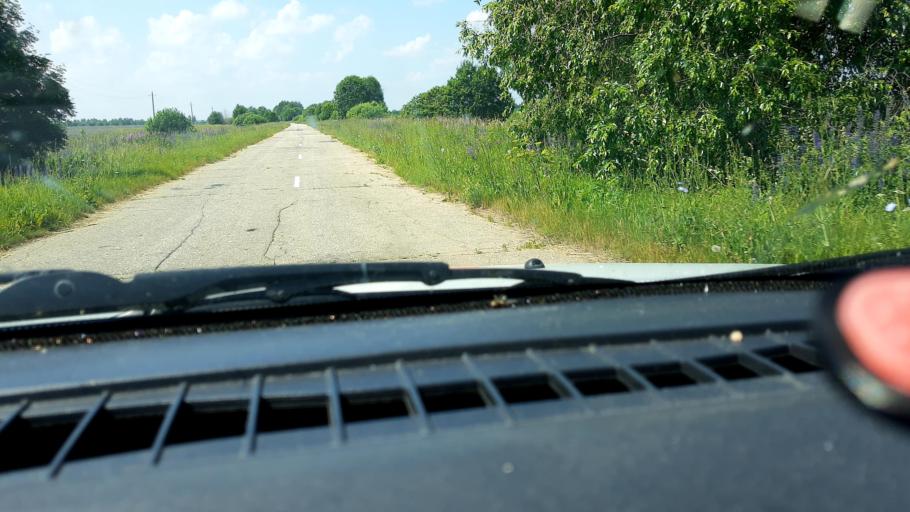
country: RU
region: Nizjnij Novgorod
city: Sharanga
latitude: 57.0626
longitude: 46.6359
